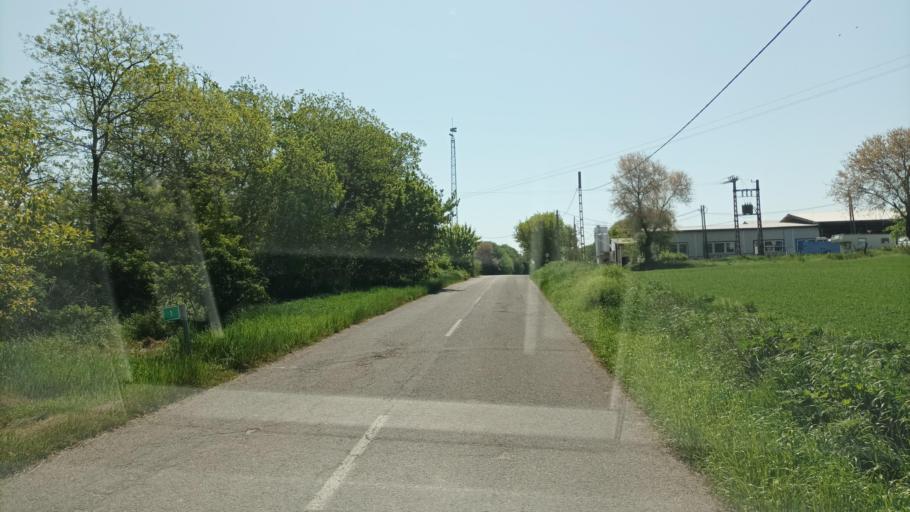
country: HU
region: Pest
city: Uri
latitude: 47.3964
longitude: 19.4930
